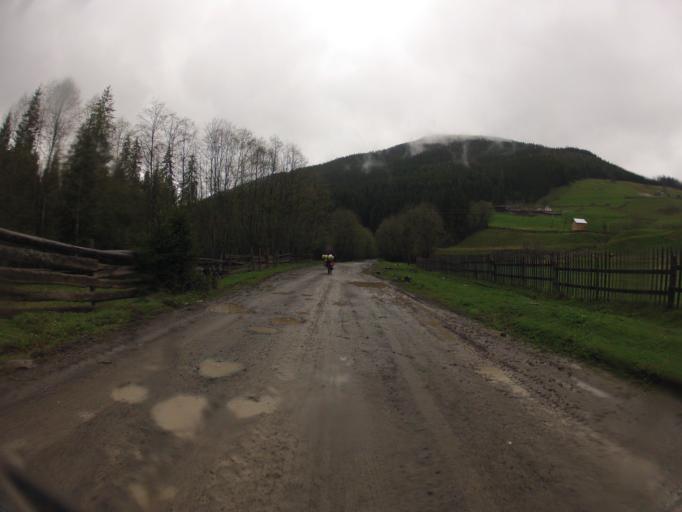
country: RO
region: Suceava
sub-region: Comuna Izvoarele Sucevei
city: Izvoarele Sucevei
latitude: 47.8330
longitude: 25.0488
